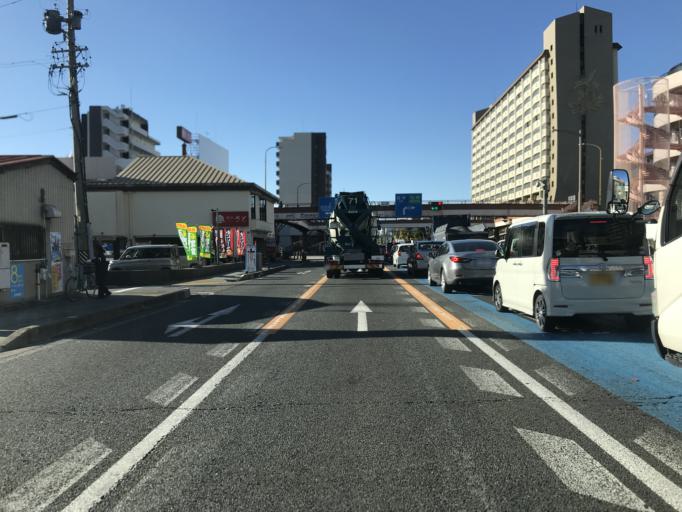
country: JP
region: Aichi
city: Nagoya-shi
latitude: 35.1875
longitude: 136.8765
